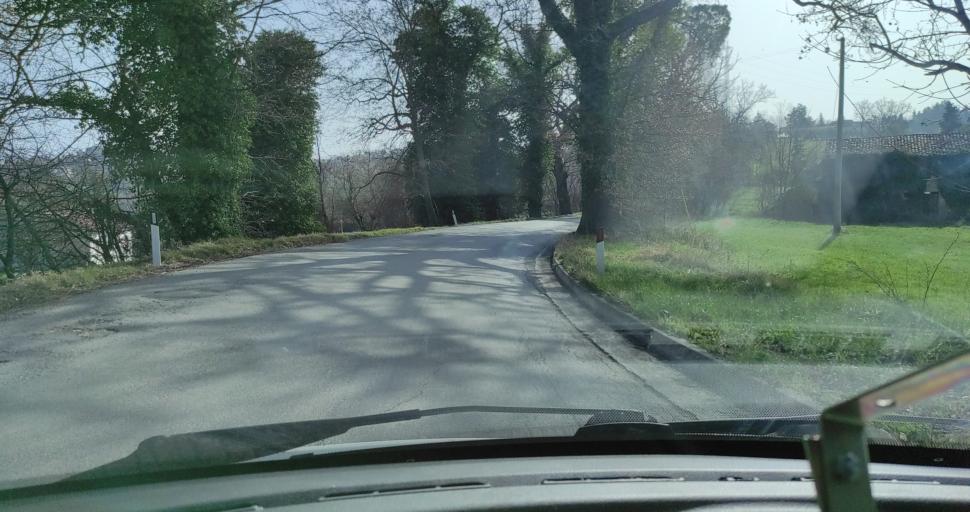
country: IT
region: The Marches
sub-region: Provincia di Macerata
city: Loro Piceno
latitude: 43.1684
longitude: 13.4021
